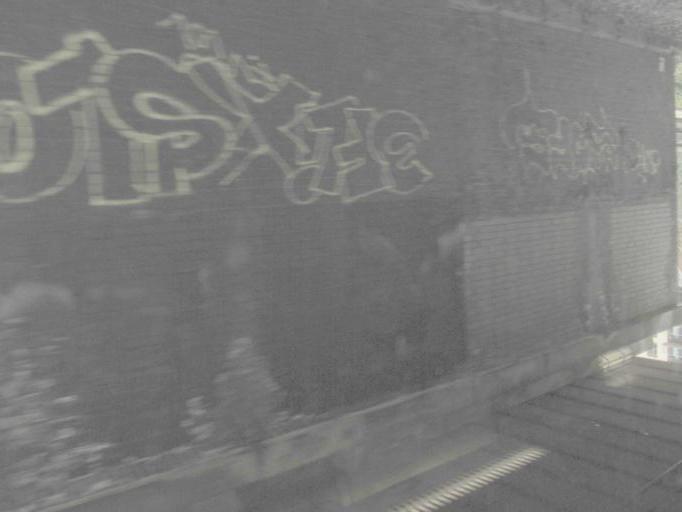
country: GB
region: England
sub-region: Greater London
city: Ealing
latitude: 51.5142
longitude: -0.3088
